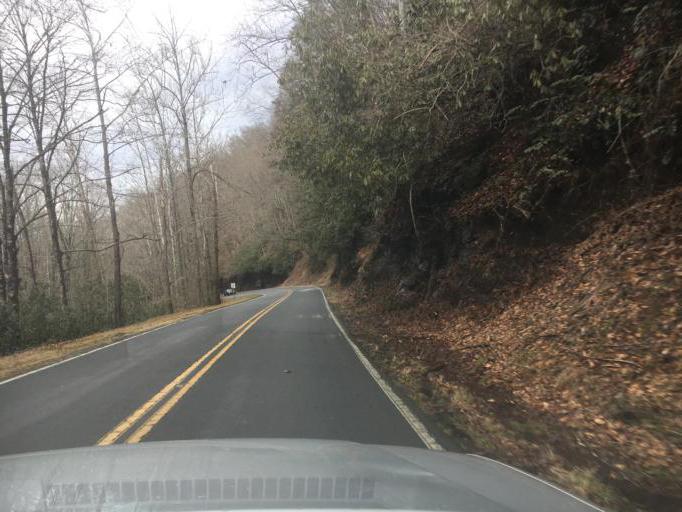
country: US
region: North Carolina
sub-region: Transylvania County
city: Brevard
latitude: 35.2826
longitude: -82.7582
